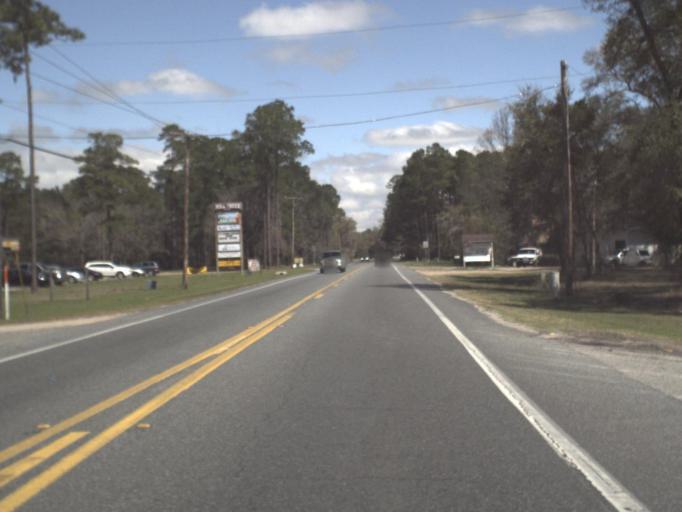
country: US
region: Florida
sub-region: Wakulla County
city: Crawfordville
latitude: 30.1665
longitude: -84.3786
